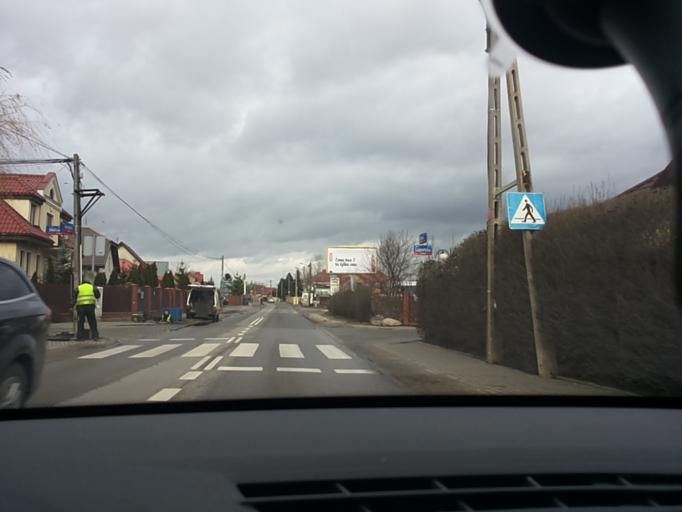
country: PL
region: Masovian Voivodeship
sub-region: Warszawa
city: Targowek
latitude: 52.3099
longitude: 21.0521
